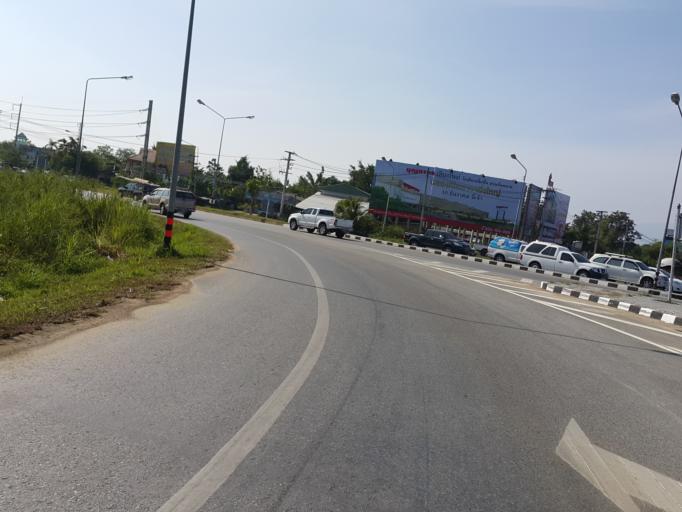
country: TH
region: Chiang Mai
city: Saraphi
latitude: 18.7529
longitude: 99.0581
